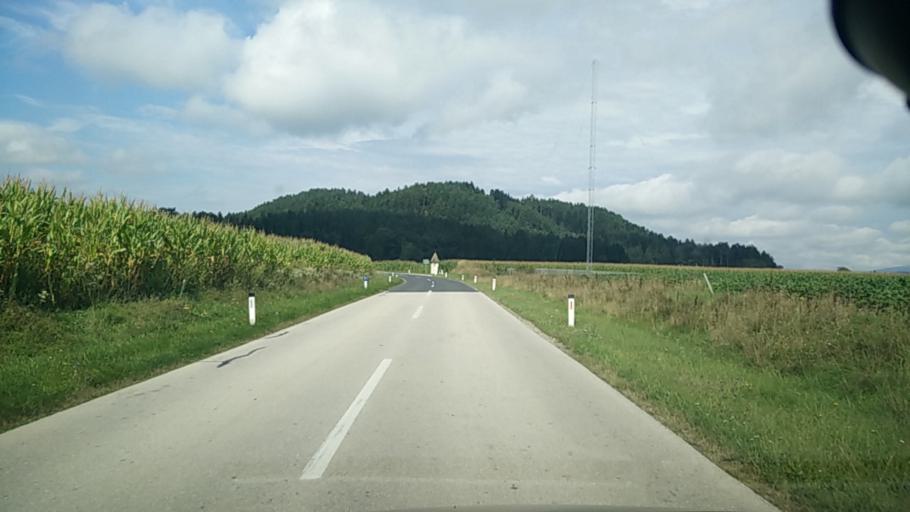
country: AT
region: Carinthia
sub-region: Politischer Bezirk Klagenfurt Land
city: Grafenstein
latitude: 46.6247
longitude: 14.5355
